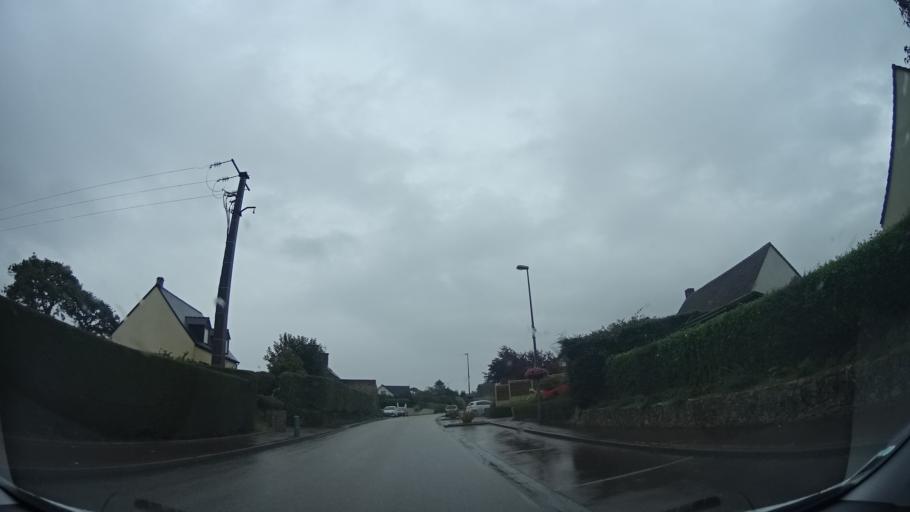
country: FR
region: Lower Normandy
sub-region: Departement de la Manche
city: Urville-Nacqueville
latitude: 49.5971
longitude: -1.7770
